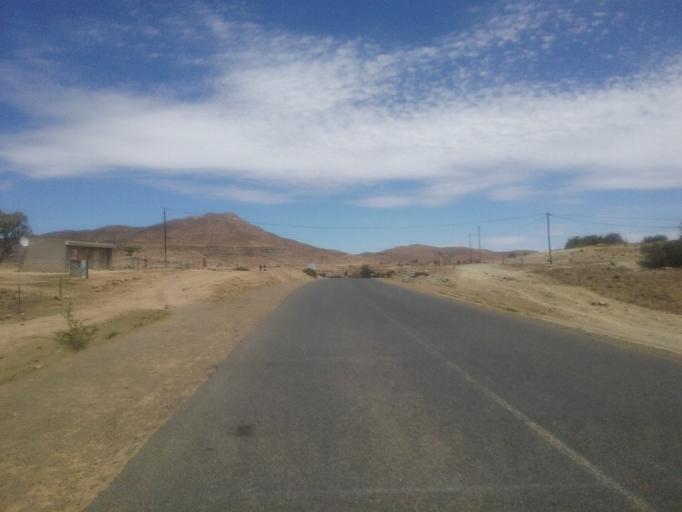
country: LS
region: Mafeteng
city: Mafeteng
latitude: -29.9512
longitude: 27.2793
